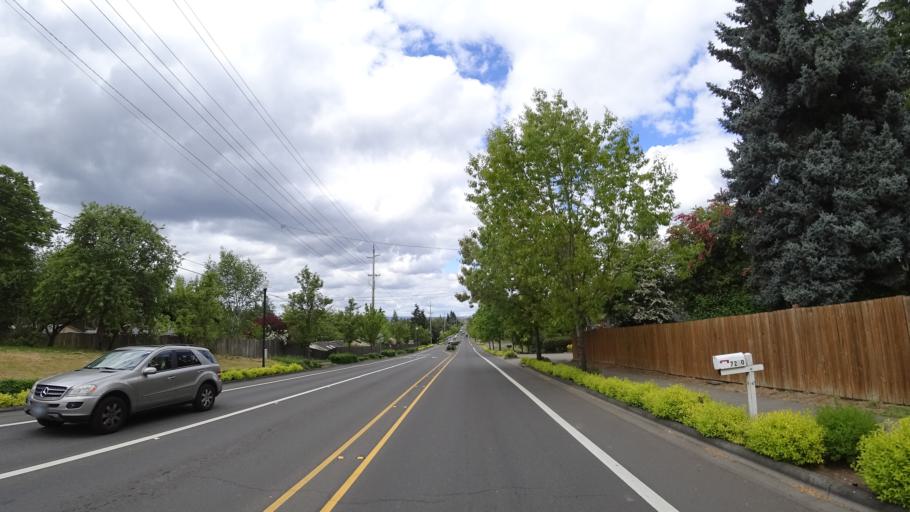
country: US
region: Oregon
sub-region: Washington County
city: Aloha
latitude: 45.4672
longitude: -122.8518
